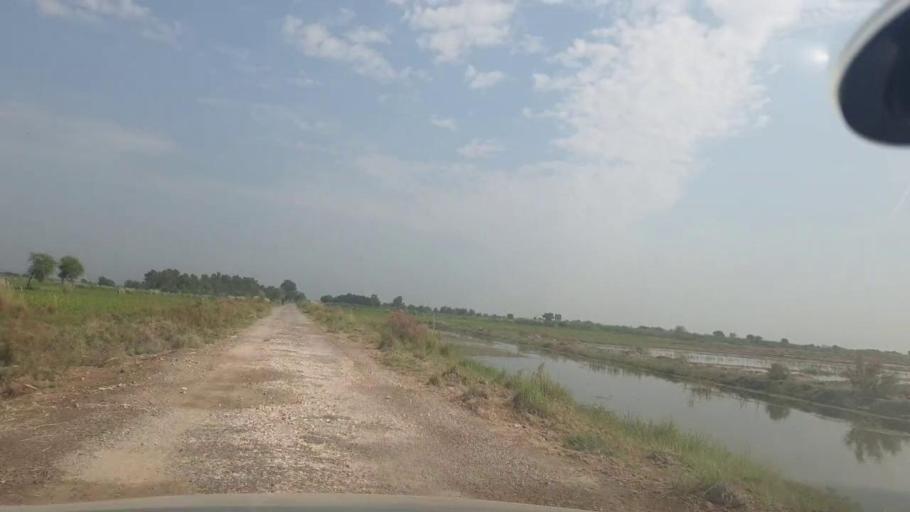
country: PK
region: Balochistan
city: Mehrabpur
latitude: 28.0483
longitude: 68.1226
